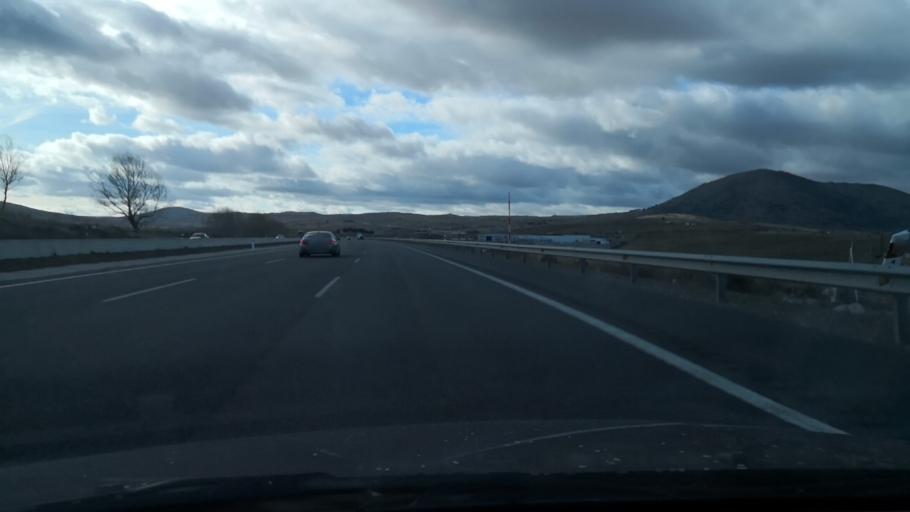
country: ES
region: Castille and Leon
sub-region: Provincia de Segovia
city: Vegas de Matute
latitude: 40.7394
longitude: -4.2236
